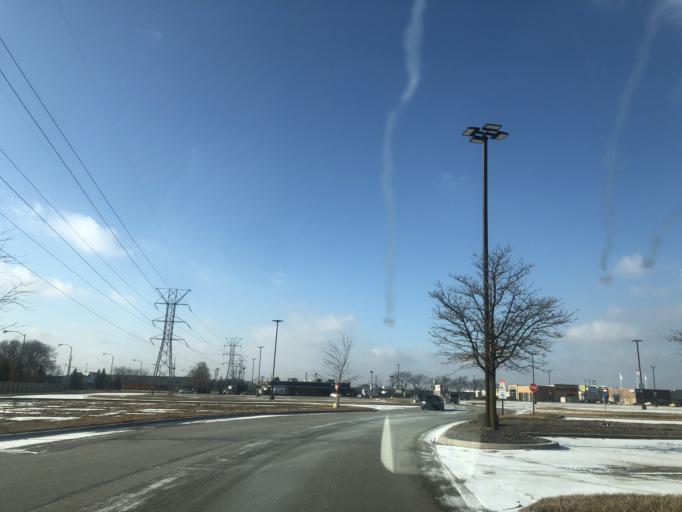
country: US
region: Illinois
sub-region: Cook County
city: Hometown
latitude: 41.7535
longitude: -87.7374
